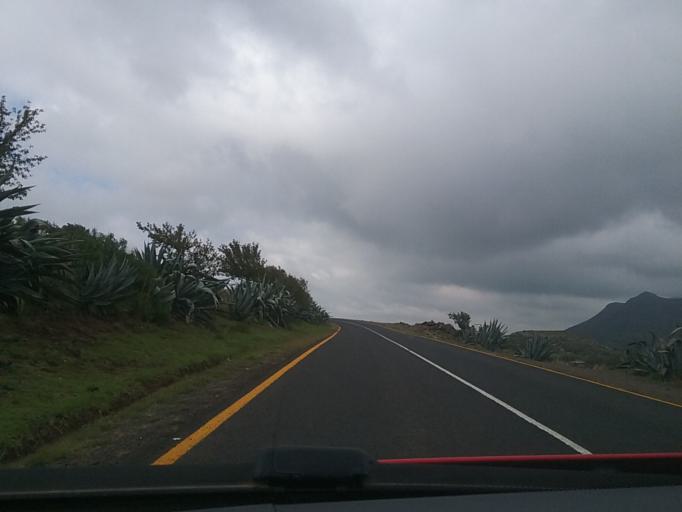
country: LS
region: Berea
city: Teyateyaneng
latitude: -29.2365
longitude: 27.8621
